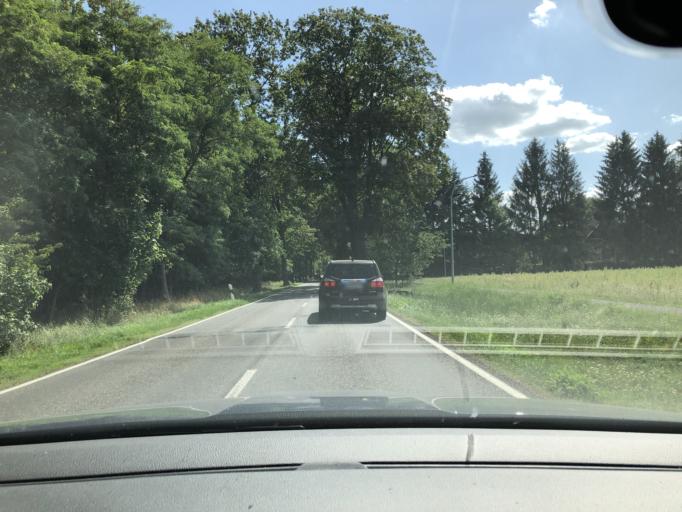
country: DE
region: Brandenburg
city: Ruthnick
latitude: 52.8780
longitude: 13.0038
